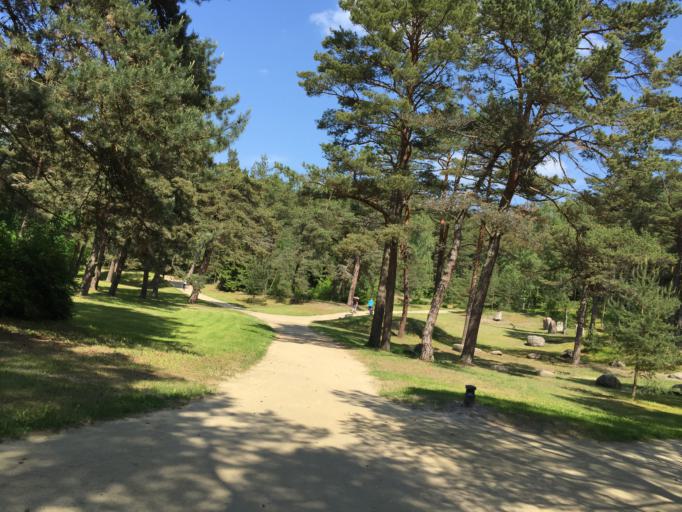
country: LT
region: Klaipedos apskritis
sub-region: Klaipeda
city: Palanga
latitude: 55.9040
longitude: 21.0526
